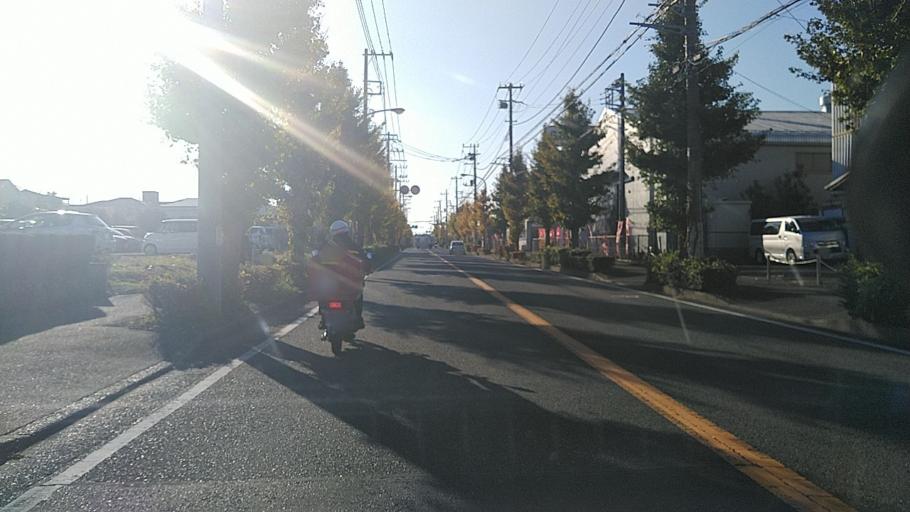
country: JP
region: Kanagawa
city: Fujisawa
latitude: 35.3792
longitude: 139.4436
